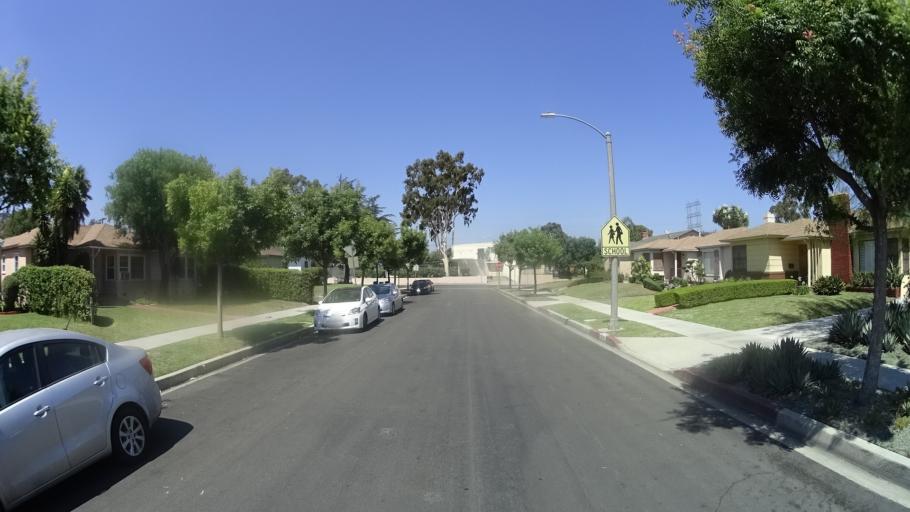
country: US
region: California
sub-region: Los Angeles County
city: Ladera Heights
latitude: 34.0225
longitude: -118.3639
